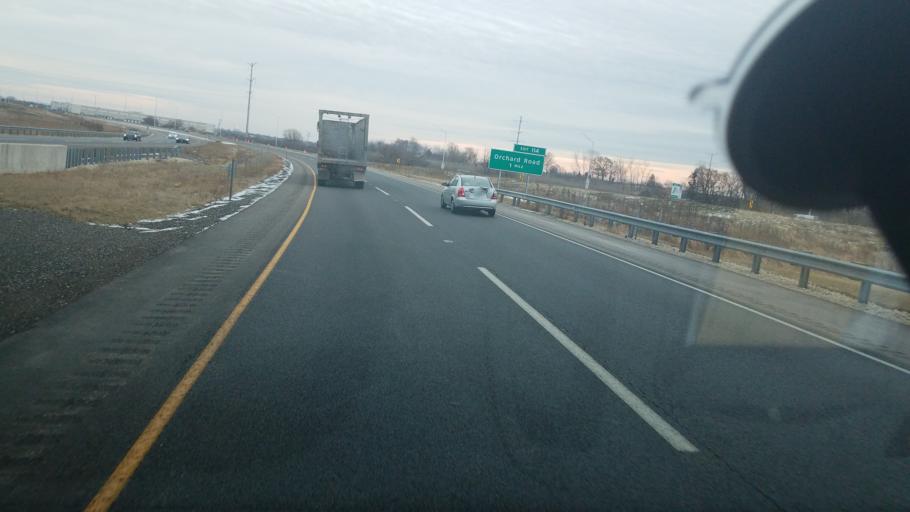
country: US
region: Illinois
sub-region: Kane County
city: Sugar Grove
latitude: 41.7958
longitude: -88.3959
